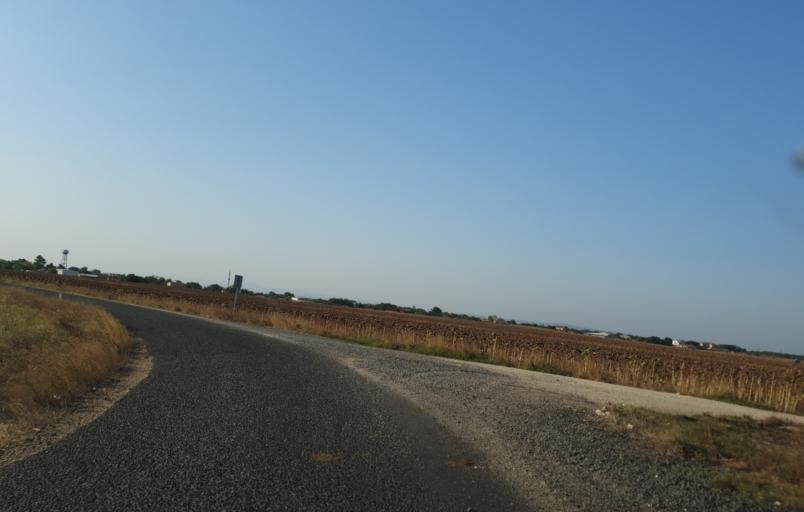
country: TR
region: Tekirdag
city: Beyazkoy
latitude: 41.4268
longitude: 27.7610
